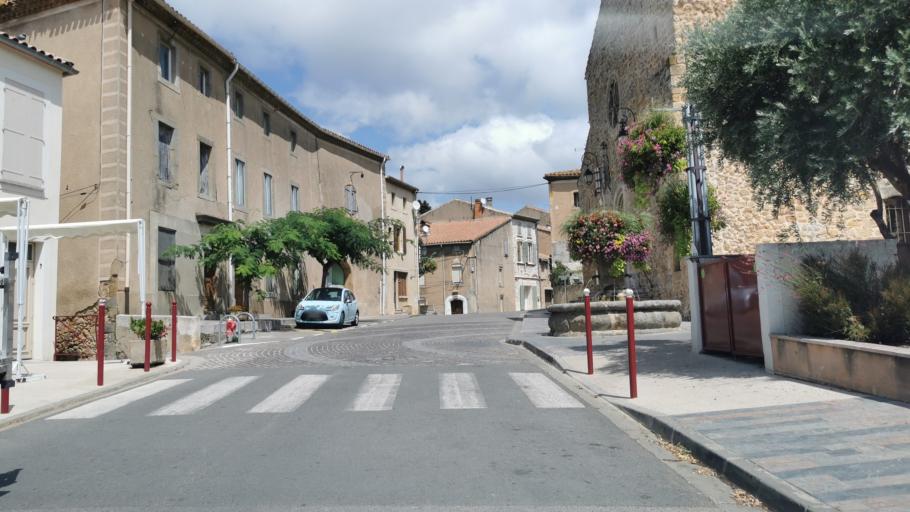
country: FR
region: Languedoc-Roussillon
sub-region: Departement de l'Aude
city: Bizanet
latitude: 43.1634
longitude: 2.8699
